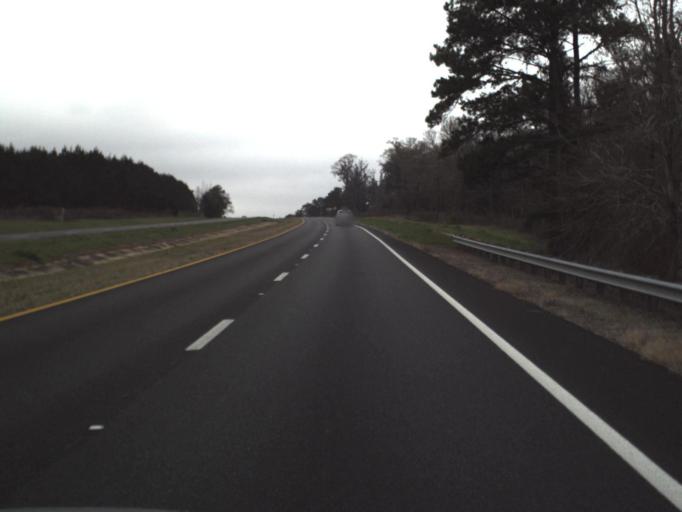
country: US
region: Florida
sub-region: Jefferson County
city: Monticello
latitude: 30.4017
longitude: -83.8835
